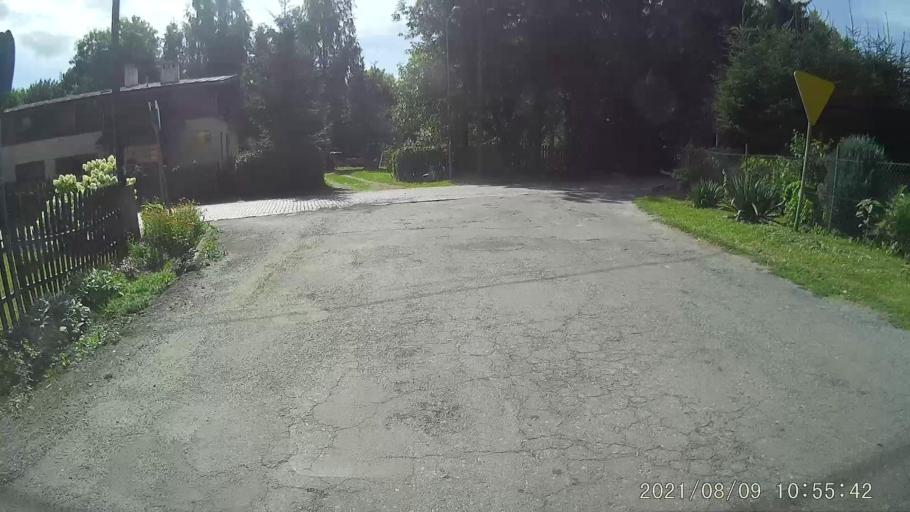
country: PL
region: Lower Silesian Voivodeship
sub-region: Powiat klodzki
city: Polanica-Zdroj
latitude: 50.4296
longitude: 16.5521
